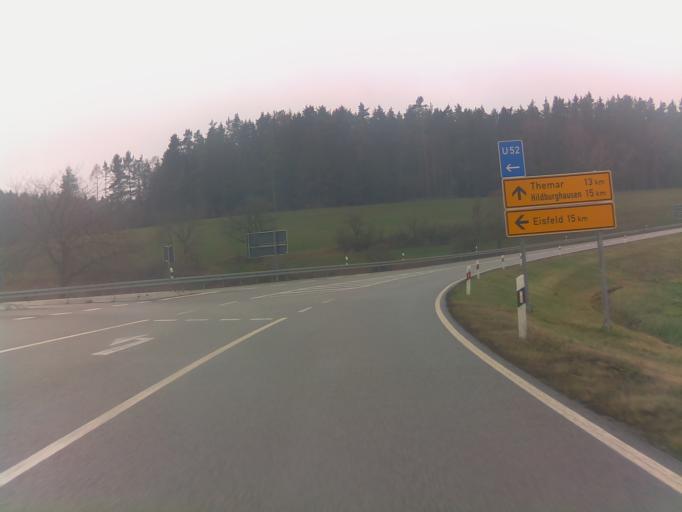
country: DE
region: Thuringia
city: Schleusingen
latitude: 50.4959
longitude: 10.7746
